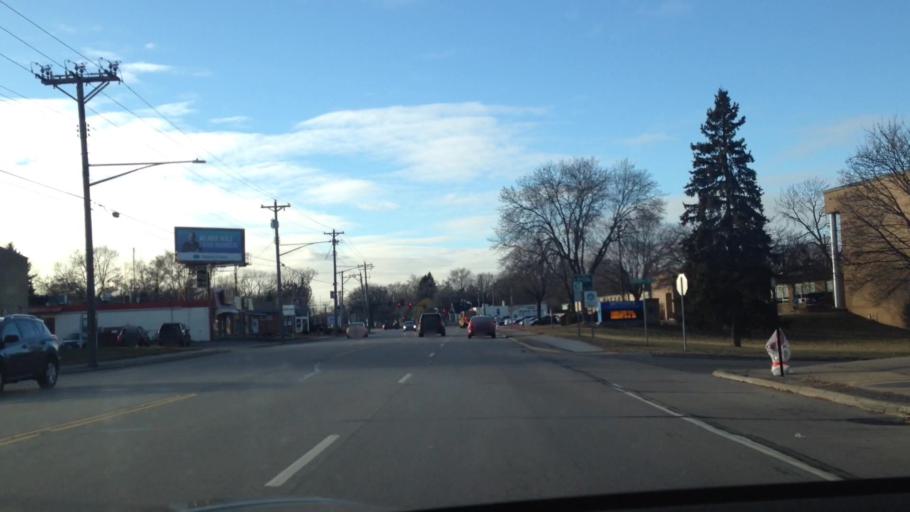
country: US
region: Minnesota
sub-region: Hennepin County
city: Crystal
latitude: 45.0324
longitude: -93.3572
